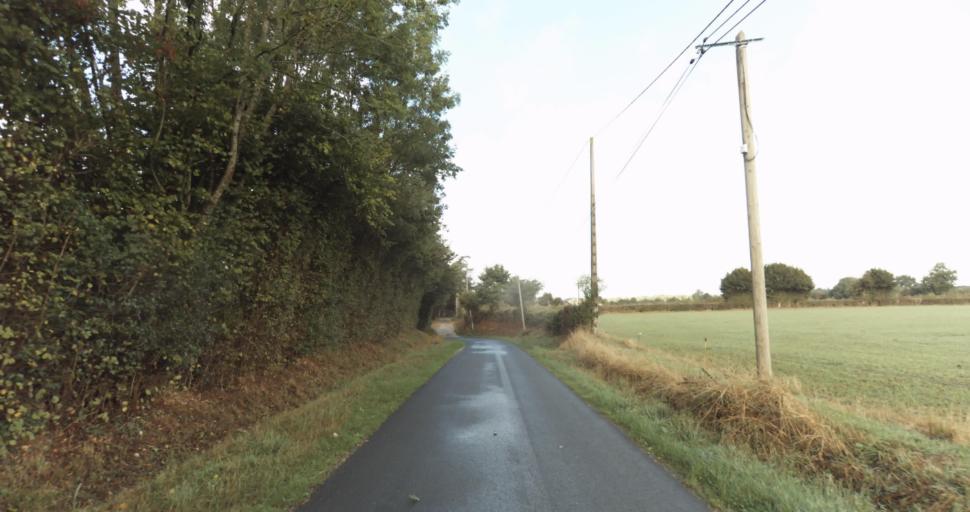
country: FR
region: Lower Normandy
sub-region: Departement de l'Orne
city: Gace
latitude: 48.8803
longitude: 0.3186
